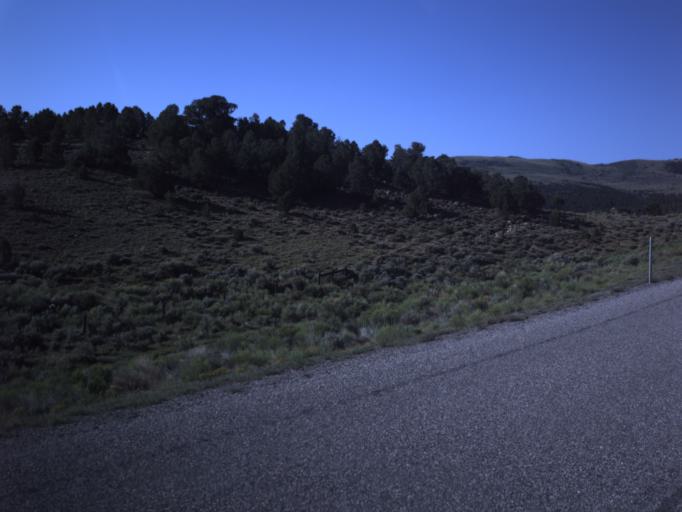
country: US
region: Utah
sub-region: Wayne County
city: Loa
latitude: 38.6251
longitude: -111.4509
